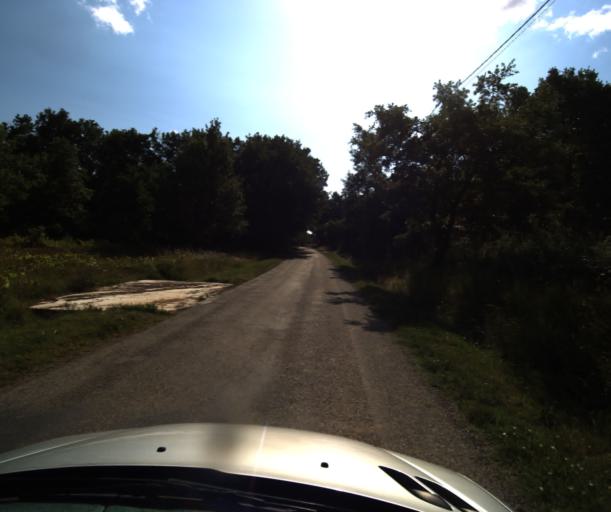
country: FR
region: Midi-Pyrenees
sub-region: Departement du Tarn-et-Garonne
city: Finhan
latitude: 43.9122
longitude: 1.2647
